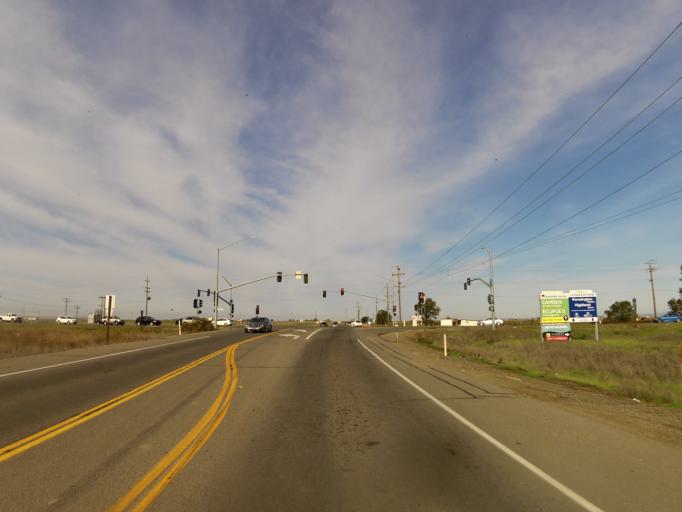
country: US
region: California
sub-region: Sacramento County
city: Wilton
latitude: 38.5050
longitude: -121.2424
